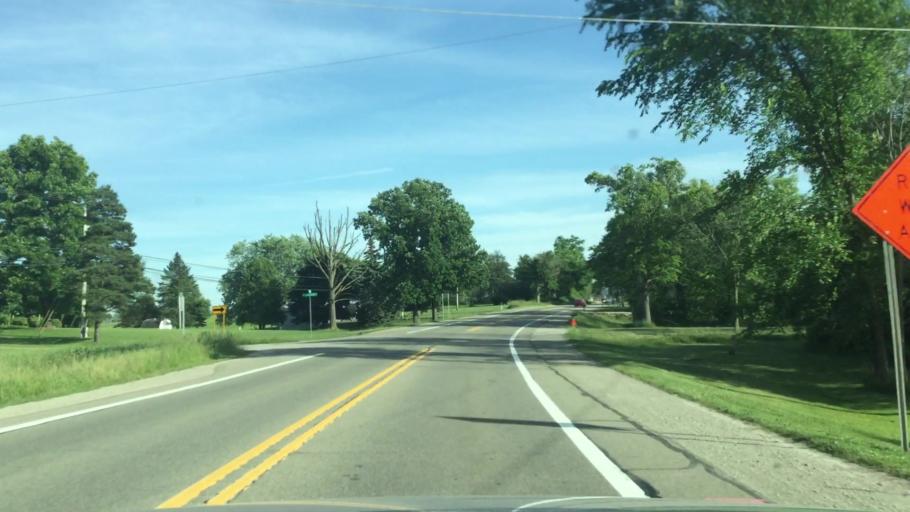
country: US
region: Michigan
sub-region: Genesee County
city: Davison
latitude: 42.9977
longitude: -83.5076
